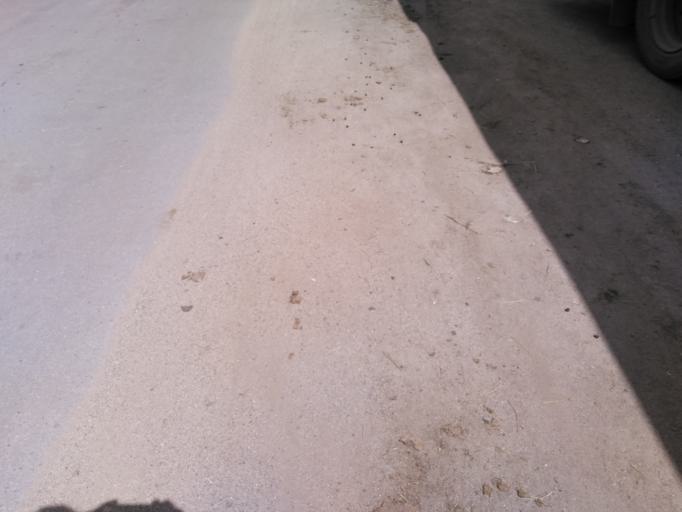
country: RU
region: Bashkortostan
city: Akhunovo
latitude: 54.2098
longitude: 59.6070
